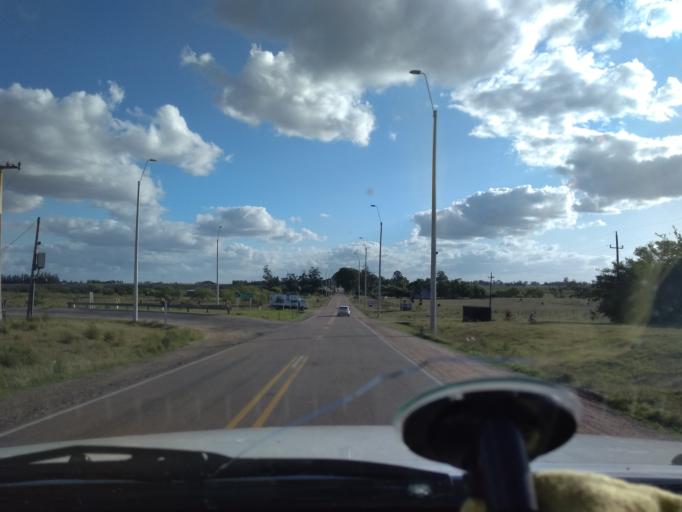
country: UY
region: Canelones
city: Tala
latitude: -34.3621
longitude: -55.7766
